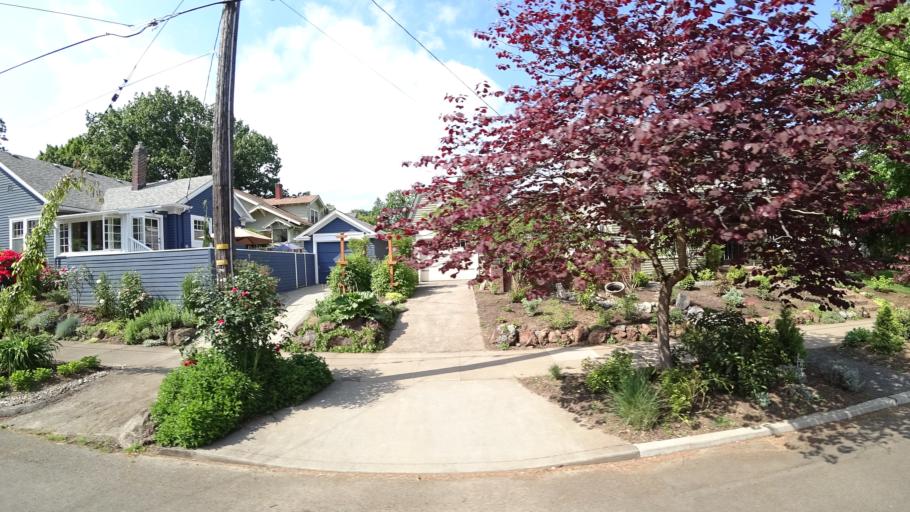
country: US
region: Oregon
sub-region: Multnomah County
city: Portland
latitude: 45.5467
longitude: -122.6477
